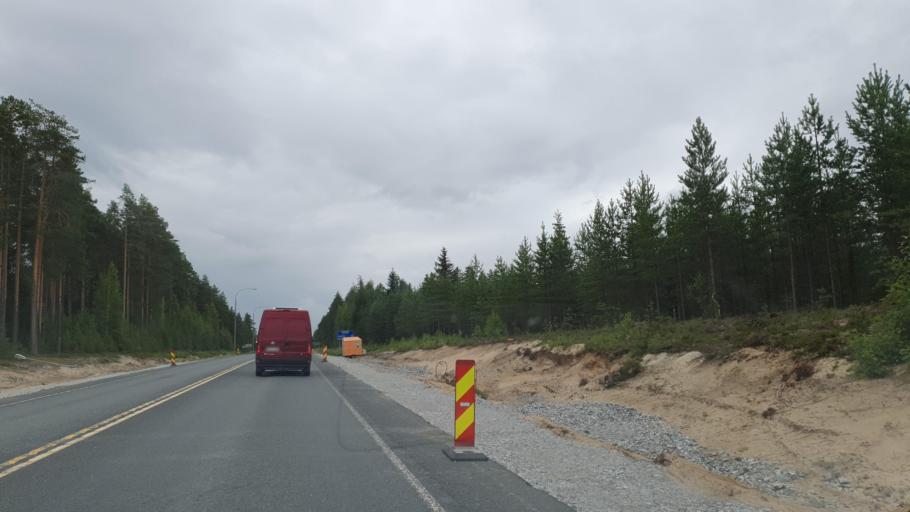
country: FI
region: Northern Savo
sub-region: Ylae-Savo
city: Lapinlahti
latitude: 63.2707
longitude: 27.4627
